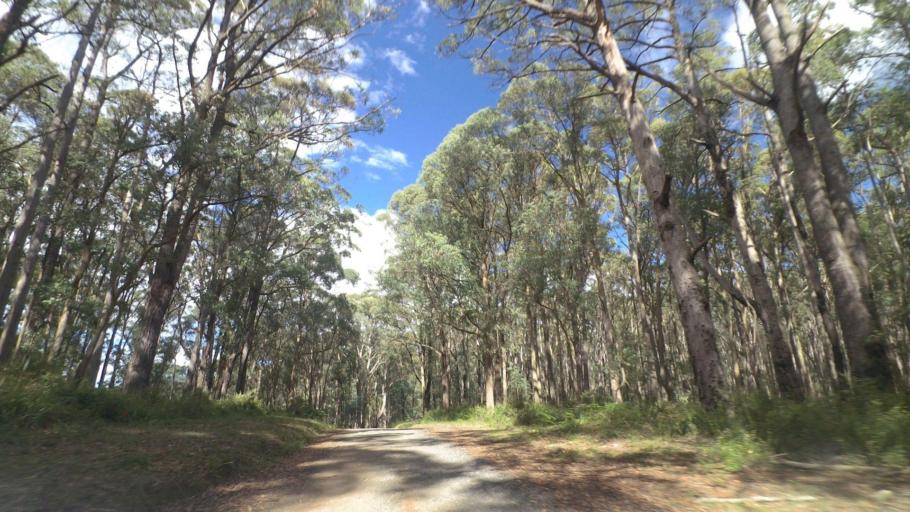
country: AU
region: Victoria
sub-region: Cardinia
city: Gembrook
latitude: -37.9082
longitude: 145.6140
